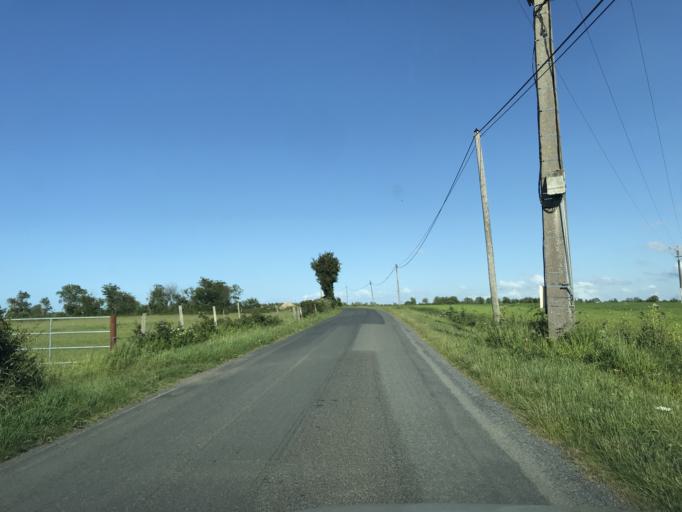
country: FR
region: Lower Normandy
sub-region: Departement du Calvados
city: Grandcamp-Maisy
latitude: 49.3806
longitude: -1.0702
